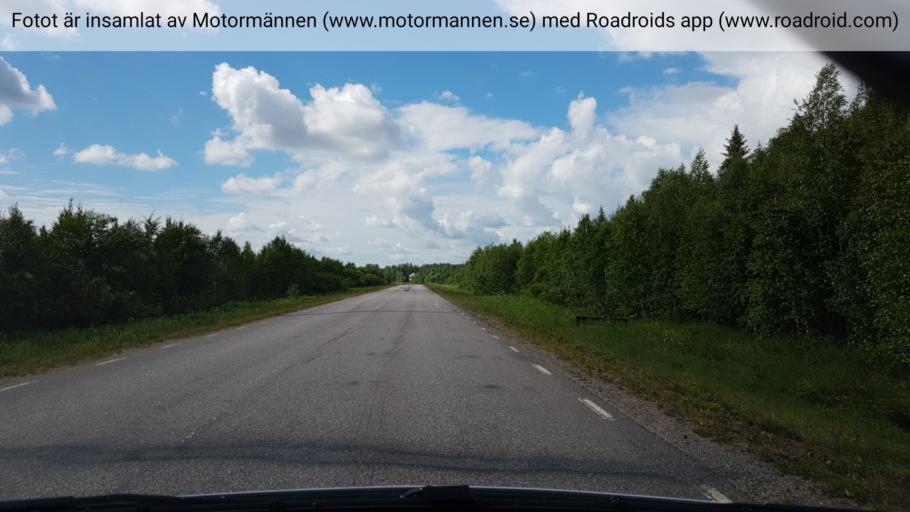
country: FI
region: Lapland
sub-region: Torniolaakso
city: Pello
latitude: 66.8072
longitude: 23.9063
